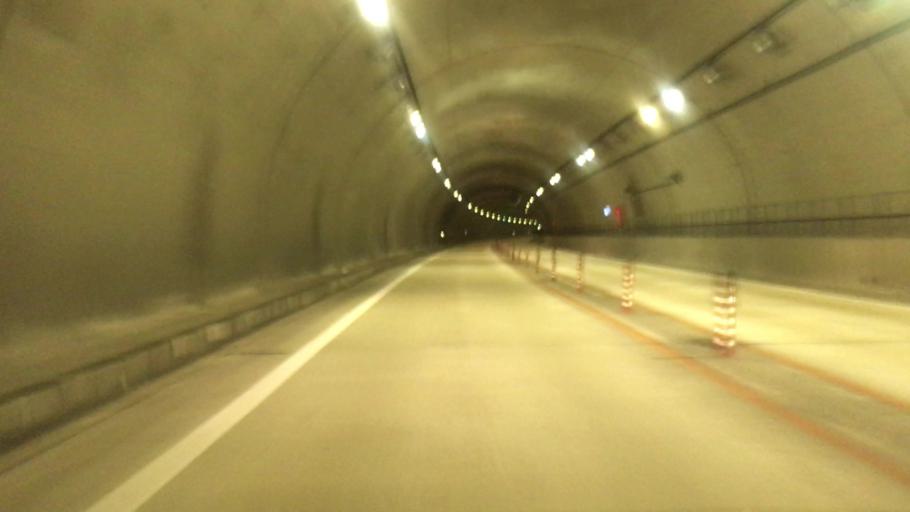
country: JP
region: Hyogo
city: Toyooka
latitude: 35.3466
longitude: 134.7806
